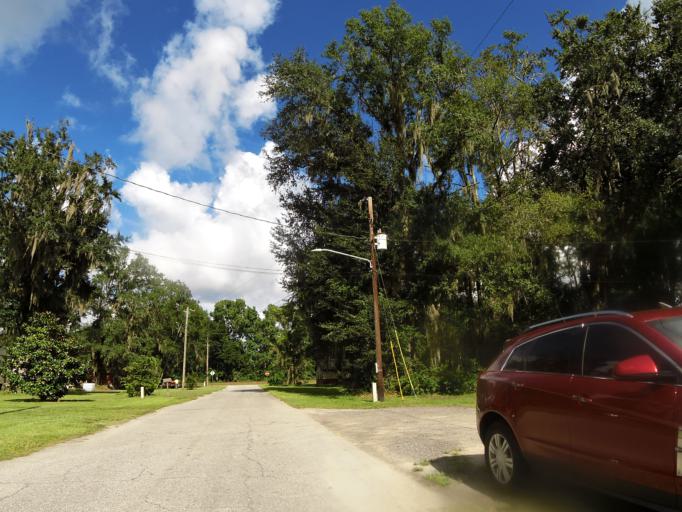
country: US
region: Georgia
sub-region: Camden County
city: Kingsland
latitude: 30.8065
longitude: -81.6939
